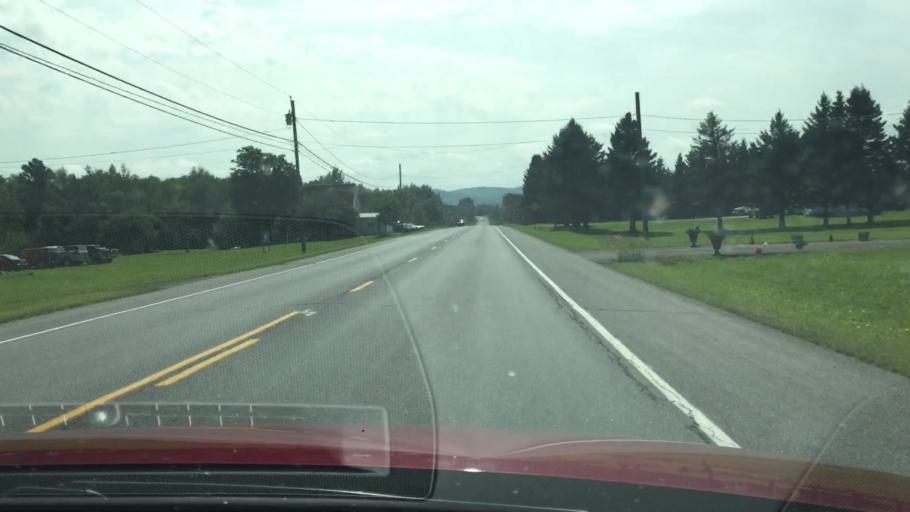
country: US
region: Maine
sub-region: Aroostook County
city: Easton
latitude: 46.5741
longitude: -67.9534
